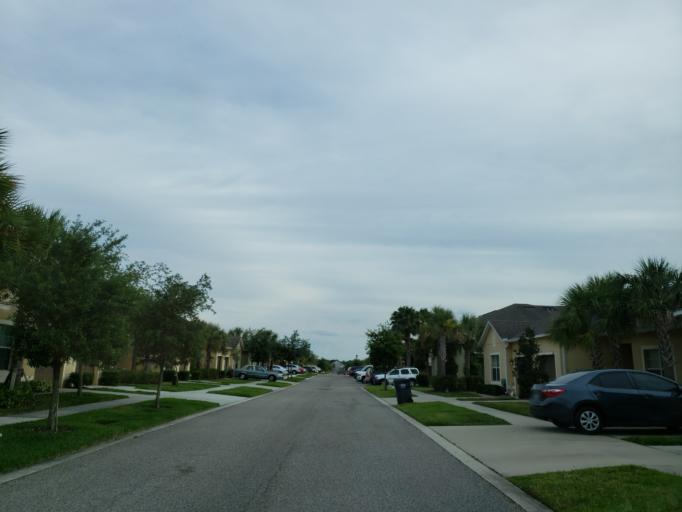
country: US
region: Florida
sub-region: Hillsborough County
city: Ruskin
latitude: 27.7333
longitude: -82.4069
